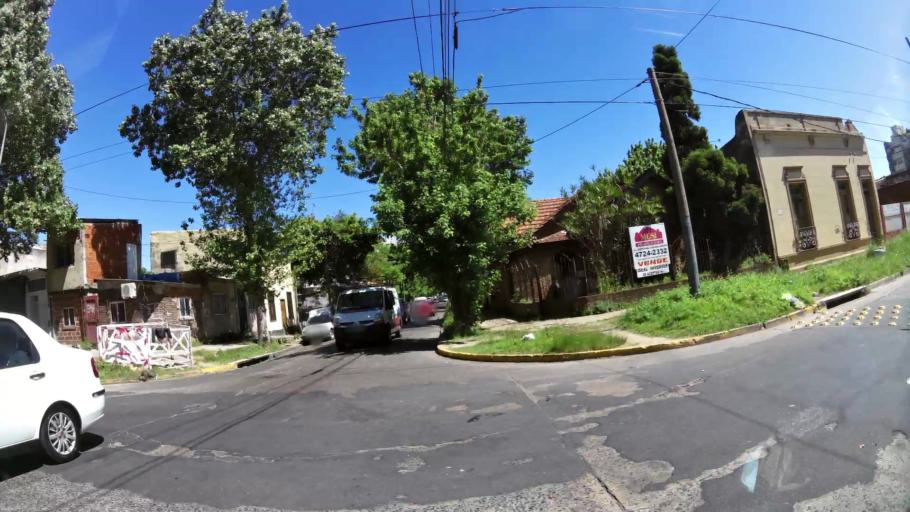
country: AR
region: Buenos Aires
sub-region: Partido de General San Martin
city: General San Martin
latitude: -34.5787
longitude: -58.5302
